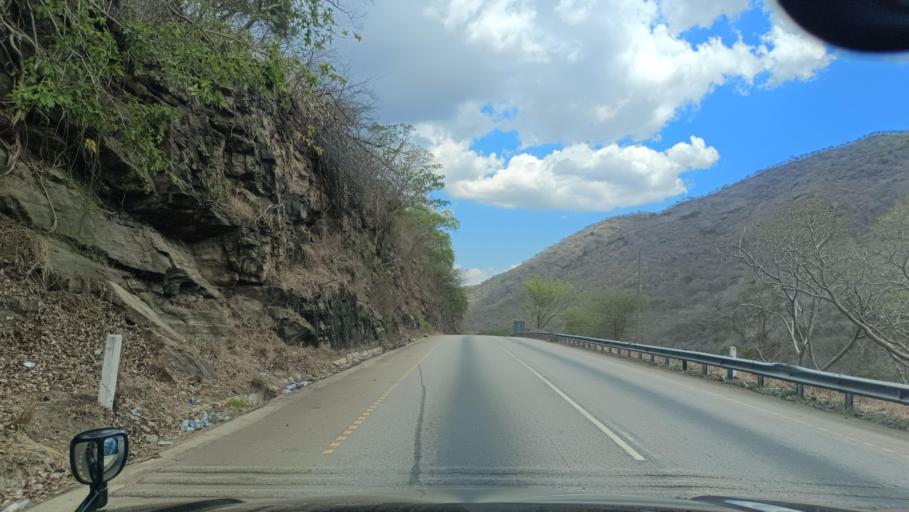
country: TZ
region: Morogoro
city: Kidatu
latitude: -7.5735
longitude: 36.7404
